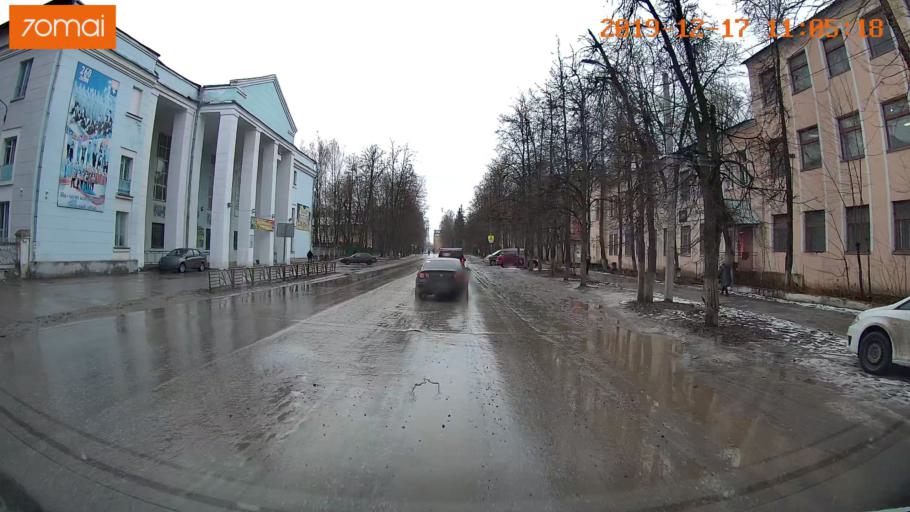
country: RU
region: Vladimir
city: Gus'-Khrustal'nyy
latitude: 55.6217
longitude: 40.6432
